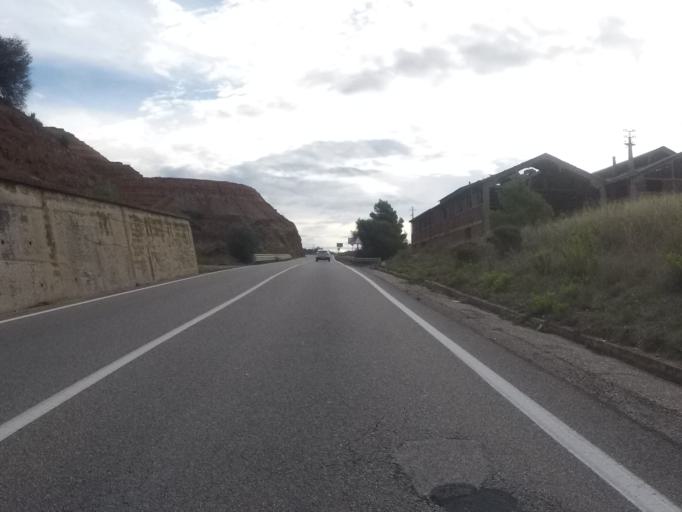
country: IT
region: Sardinia
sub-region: Provincia di Carbonia-Iglesias
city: Iglesias
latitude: 39.2975
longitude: 8.5028
